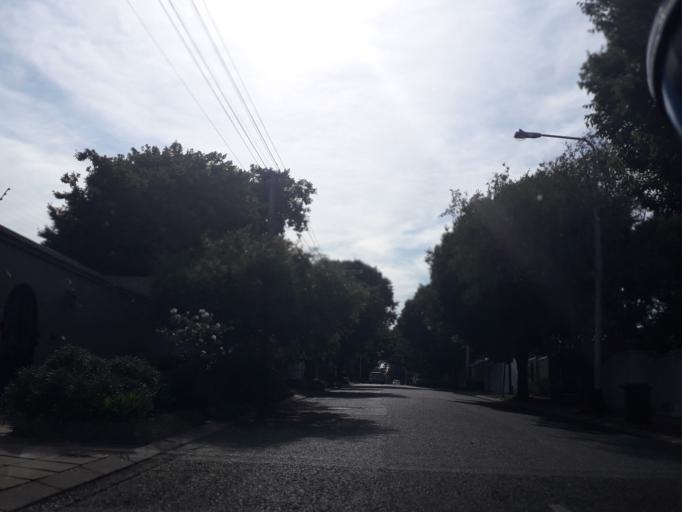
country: ZA
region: Gauteng
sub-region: City of Johannesburg Metropolitan Municipality
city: Johannesburg
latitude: -26.1407
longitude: 28.0197
